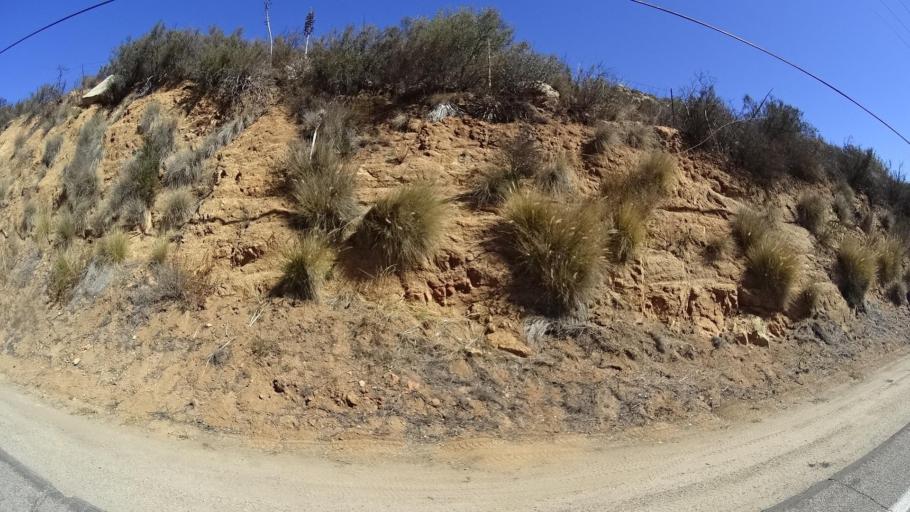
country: US
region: California
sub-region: San Diego County
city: Alpine
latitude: 32.7134
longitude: -116.7478
